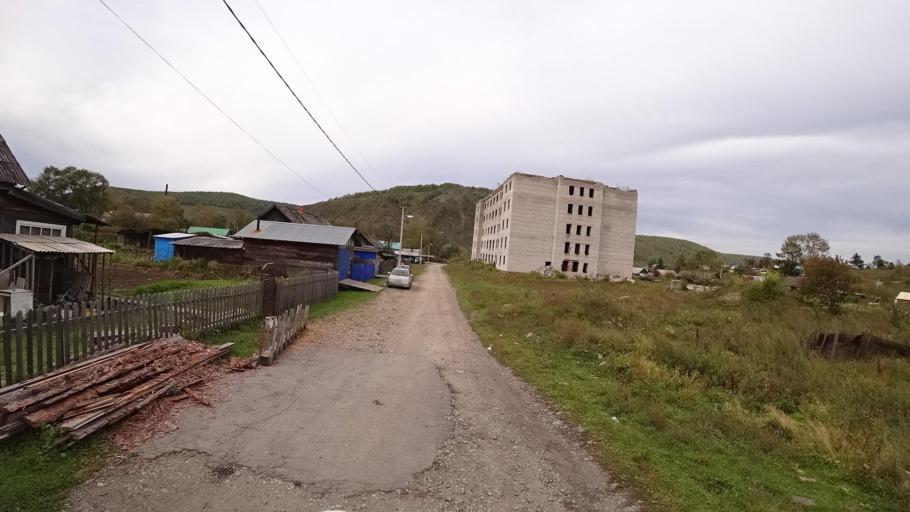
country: RU
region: Jewish Autonomous Oblast
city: Khingansk
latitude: 49.1265
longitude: 131.1991
